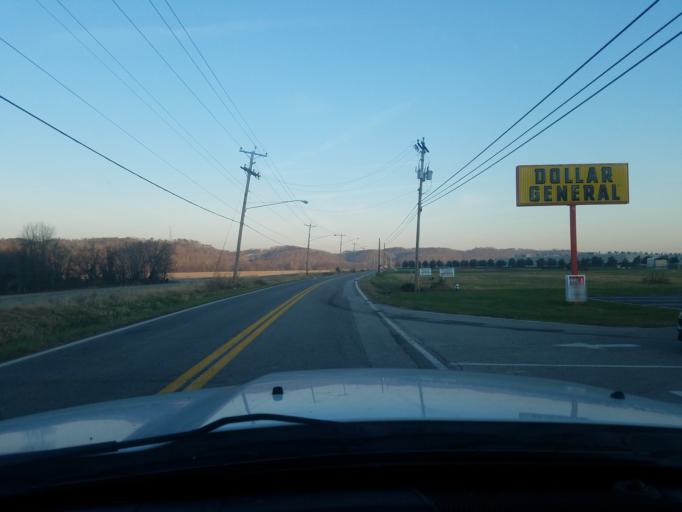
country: US
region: West Virginia
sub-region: Putnam County
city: Buffalo
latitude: 38.5879
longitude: -81.9959
